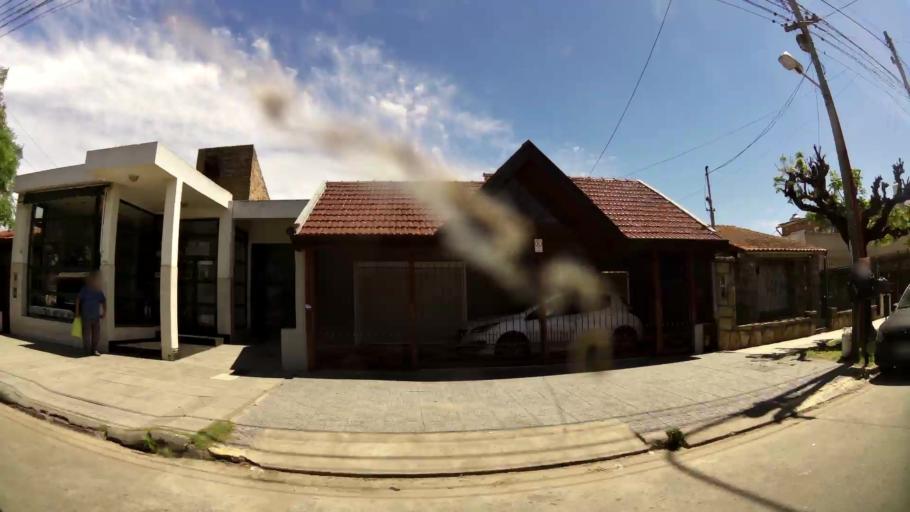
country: AR
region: Buenos Aires
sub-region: Partido de Quilmes
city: Quilmes
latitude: -34.7320
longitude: -58.3028
